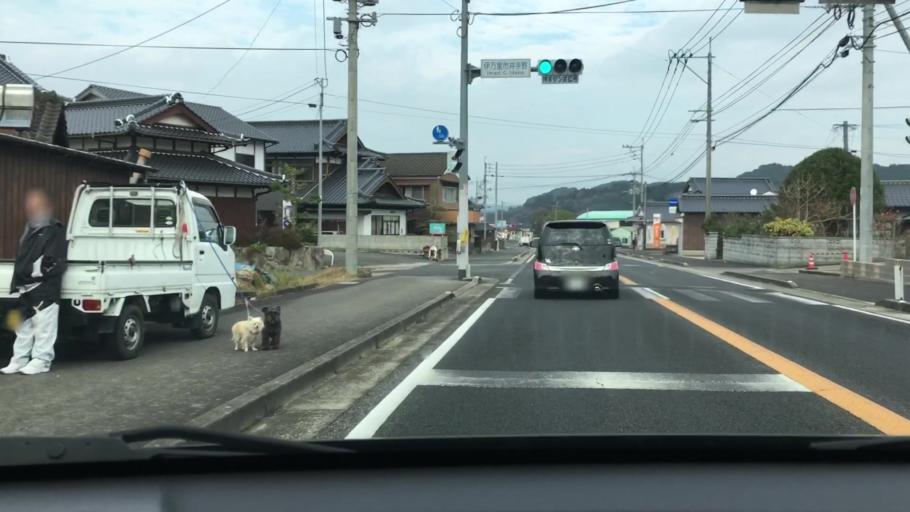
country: JP
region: Saga Prefecture
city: Imaricho-ko
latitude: 33.3109
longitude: 129.9281
